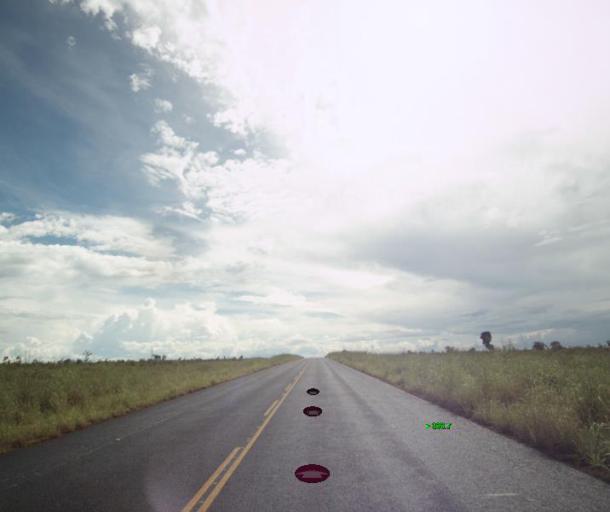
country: BR
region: Goias
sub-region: Sao Miguel Do Araguaia
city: Sao Miguel do Araguaia
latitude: -13.2963
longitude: -50.3524
